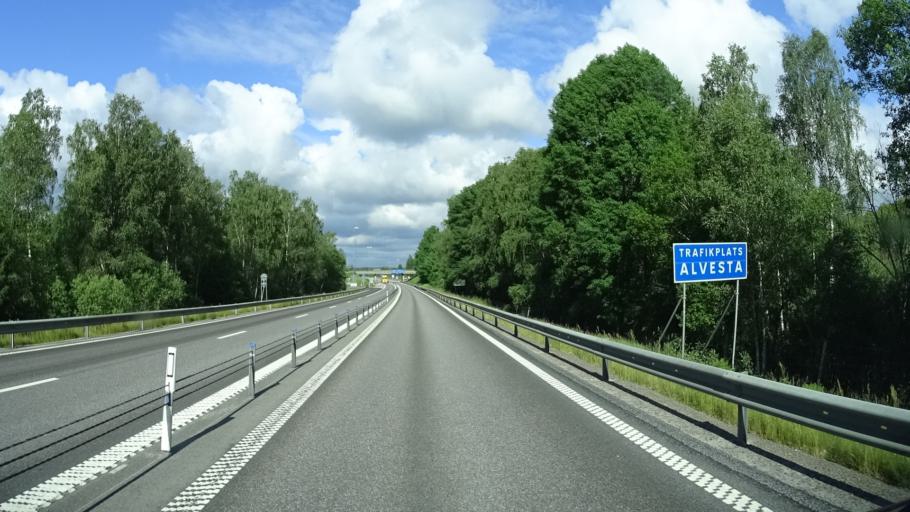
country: SE
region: Kronoberg
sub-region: Alvesta Kommun
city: Alvesta
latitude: 56.9222
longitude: 14.5634
